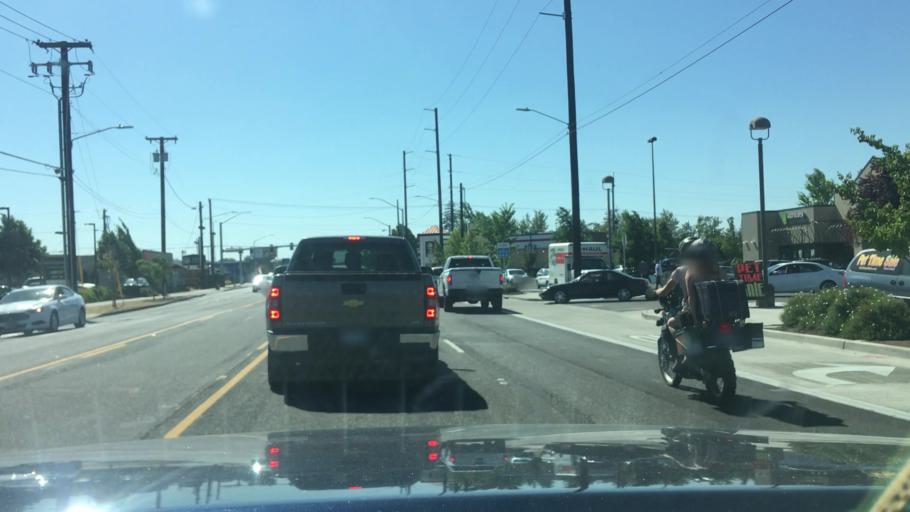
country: US
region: Oregon
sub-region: Lane County
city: Eugene
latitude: 44.0480
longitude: -123.1387
